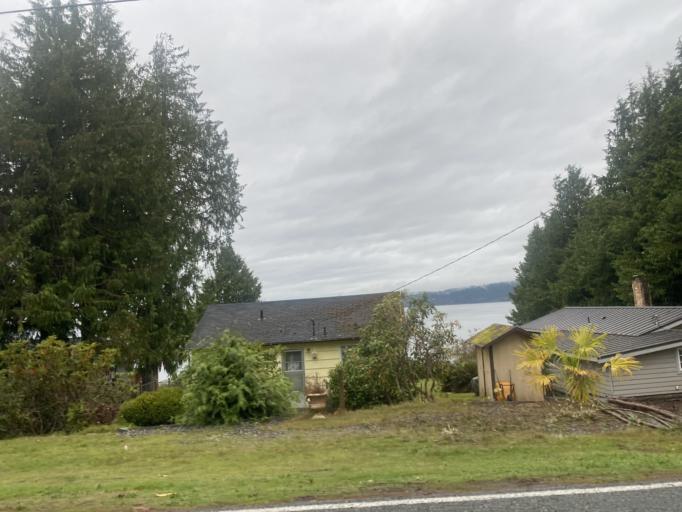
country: US
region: Washington
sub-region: Island County
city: Camano
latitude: 48.0965
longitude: -122.5151
